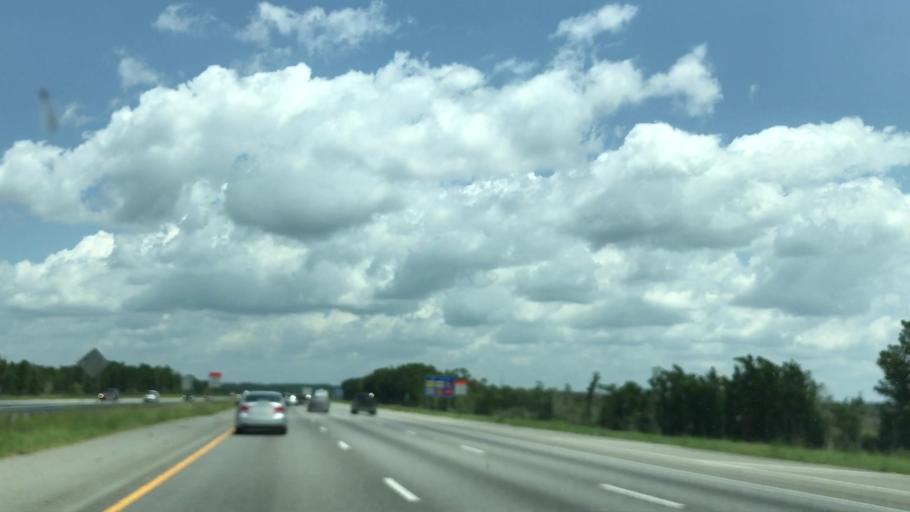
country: US
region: Georgia
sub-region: Glynn County
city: Dock Junction
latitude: 31.1981
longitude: -81.5375
